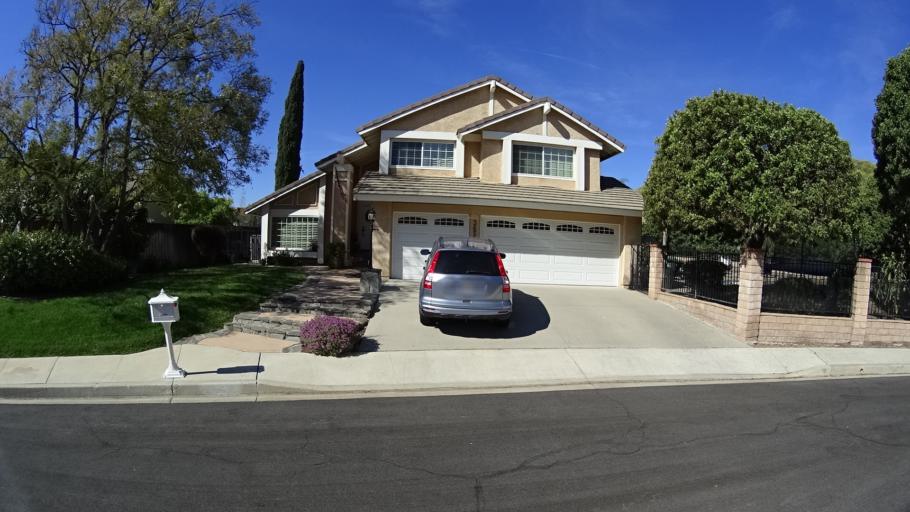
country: US
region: California
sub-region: Ventura County
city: Moorpark
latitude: 34.2294
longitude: -118.8609
